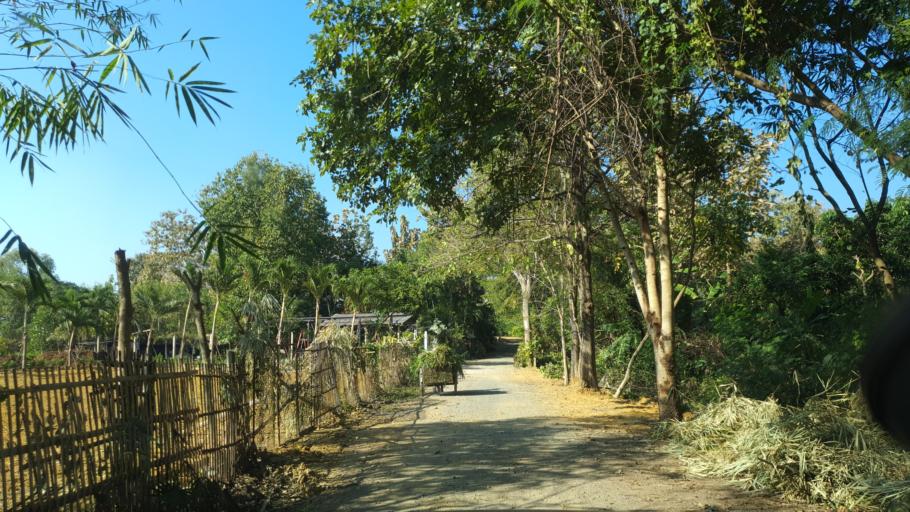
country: TH
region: Chiang Mai
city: San Kamphaeng
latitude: 18.7355
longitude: 99.1664
